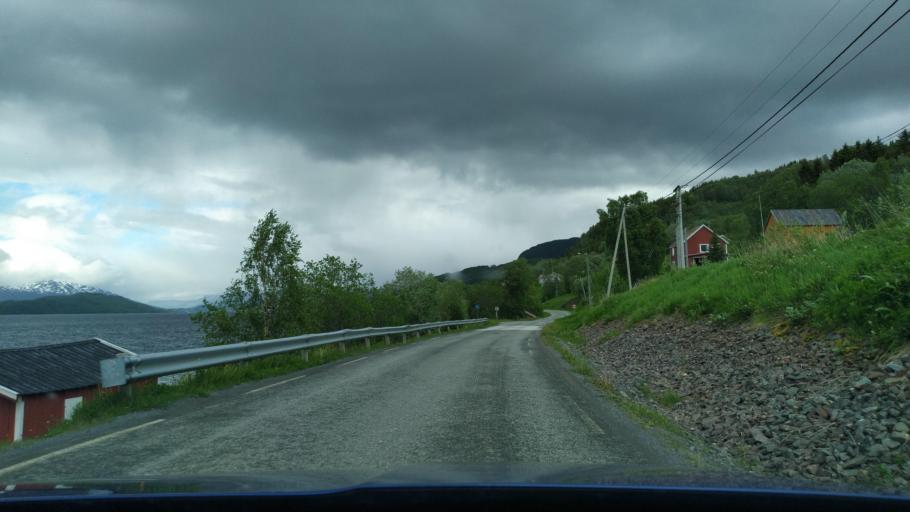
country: NO
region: Troms
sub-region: Tranoy
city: Vangsvika
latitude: 69.1299
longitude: 17.8663
